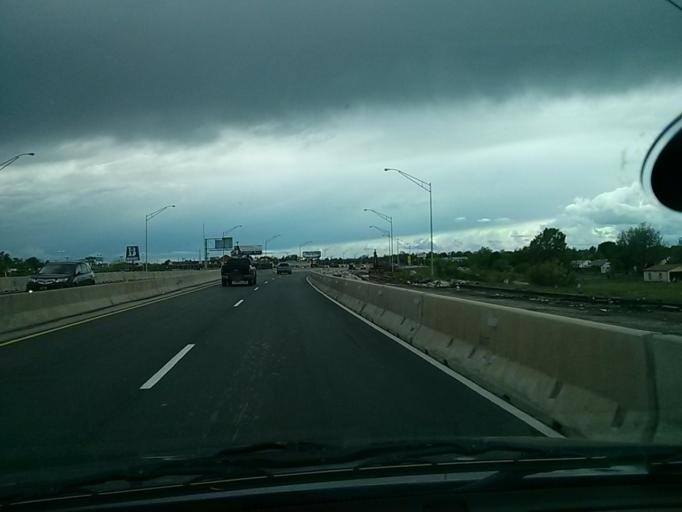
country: US
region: Oklahoma
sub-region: Tulsa County
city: Tulsa
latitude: 36.1620
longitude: -95.8944
